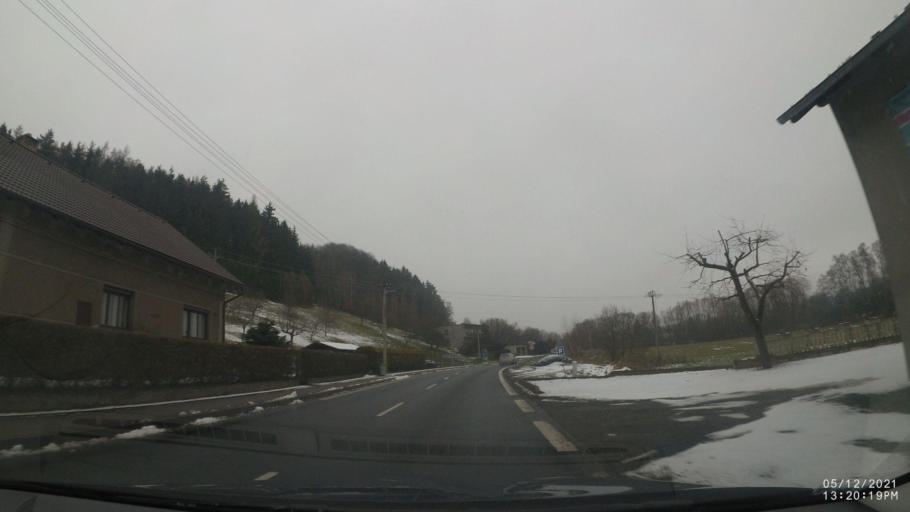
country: CZ
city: Velke Porici
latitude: 50.4490
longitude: 16.1886
